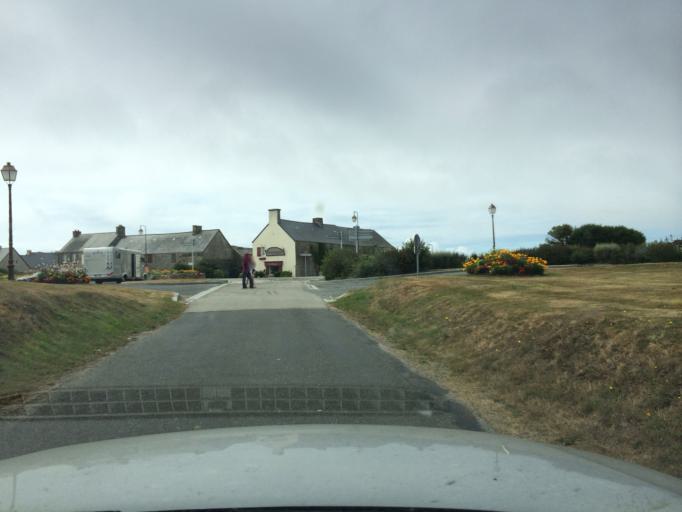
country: FR
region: Lower Normandy
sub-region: Departement de la Manche
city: Beaumont-Hague
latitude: 49.6842
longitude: -1.9049
